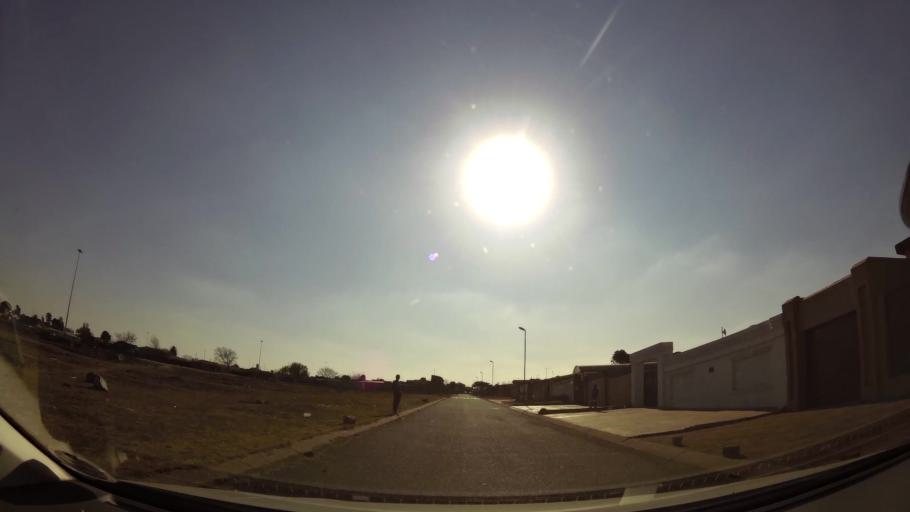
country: ZA
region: Gauteng
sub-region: City of Johannesburg Metropolitan Municipality
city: Soweto
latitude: -26.2772
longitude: 27.8737
